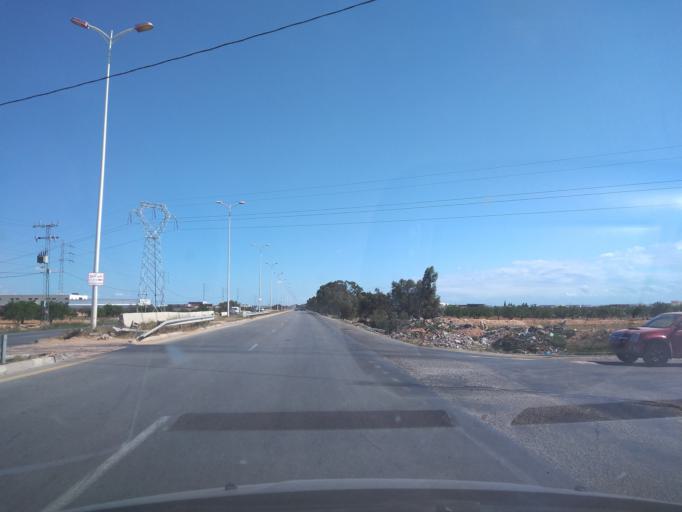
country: TN
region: Safaqis
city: Sfax
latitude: 34.8186
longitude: 10.7047
